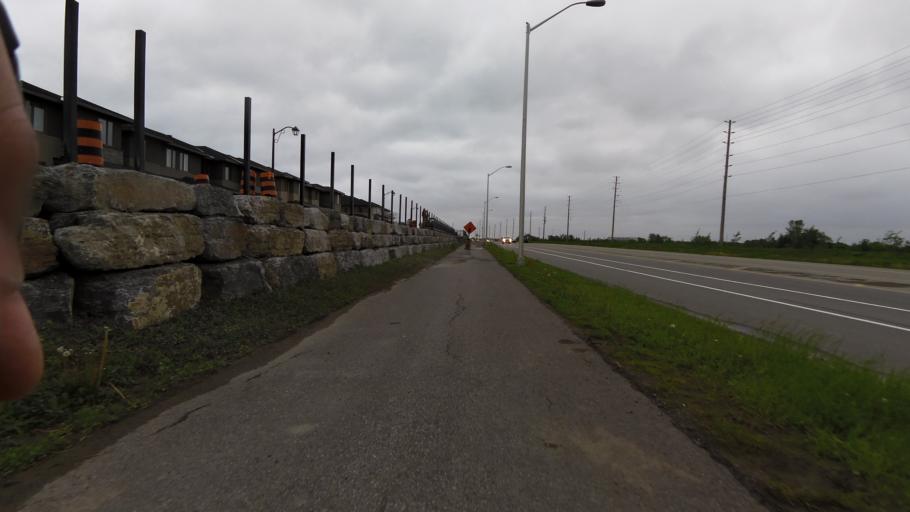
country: CA
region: Ontario
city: Bells Corners
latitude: 45.3174
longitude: -75.9437
